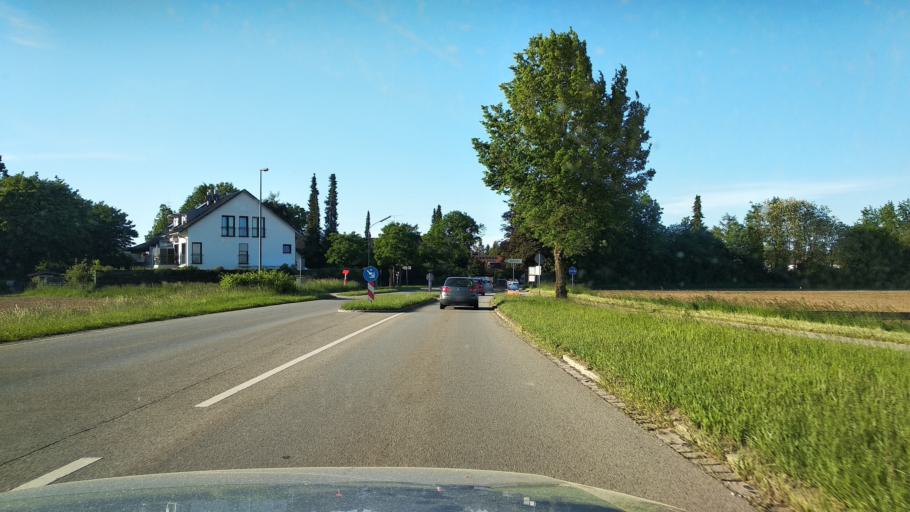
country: DE
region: Bavaria
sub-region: Upper Bavaria
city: Haar
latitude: 48.1005
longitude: 11.7312
